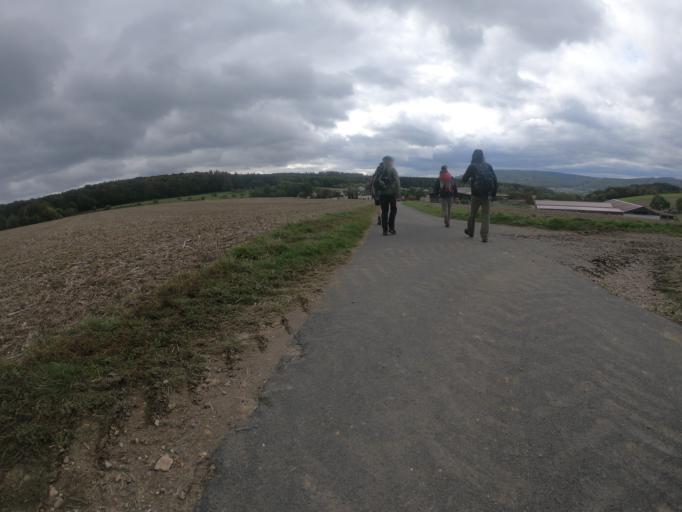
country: DE
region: Hesse
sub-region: Regierungsbezirk Darmstadt
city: Niedernhausen
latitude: 50.1978
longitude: 8.3180
